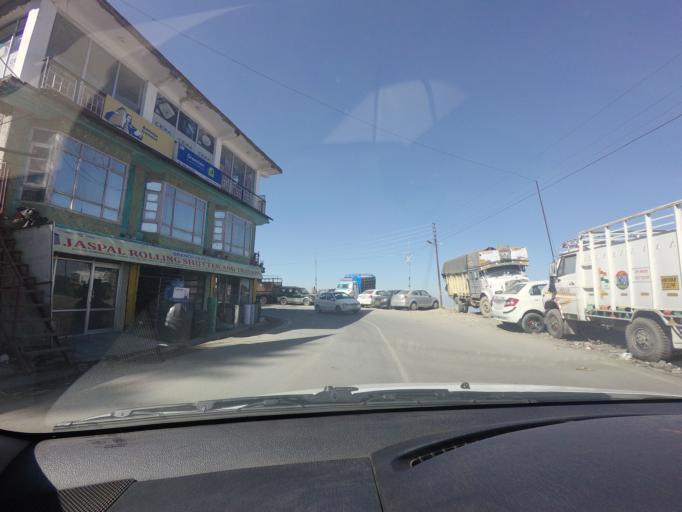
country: IN
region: Himachal Pradesh
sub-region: Shimla
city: Shimla
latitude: 31.1085
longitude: 77.2105
